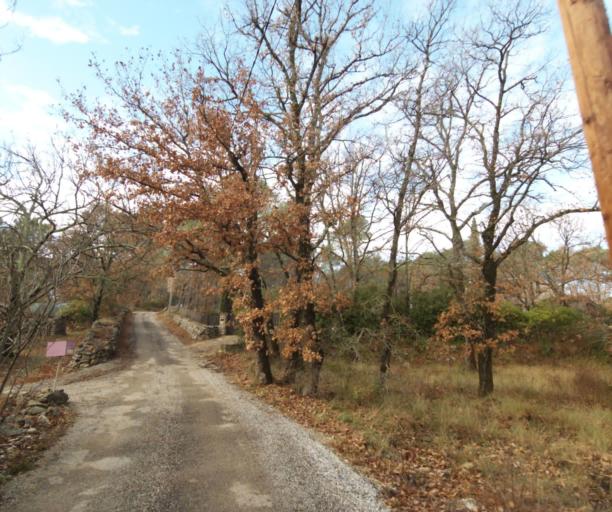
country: FR
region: Provence-Alpes-Cote d'Azur
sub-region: Departement du Var
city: Trans-en-Provence
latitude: 43.4949
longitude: 6.4591
